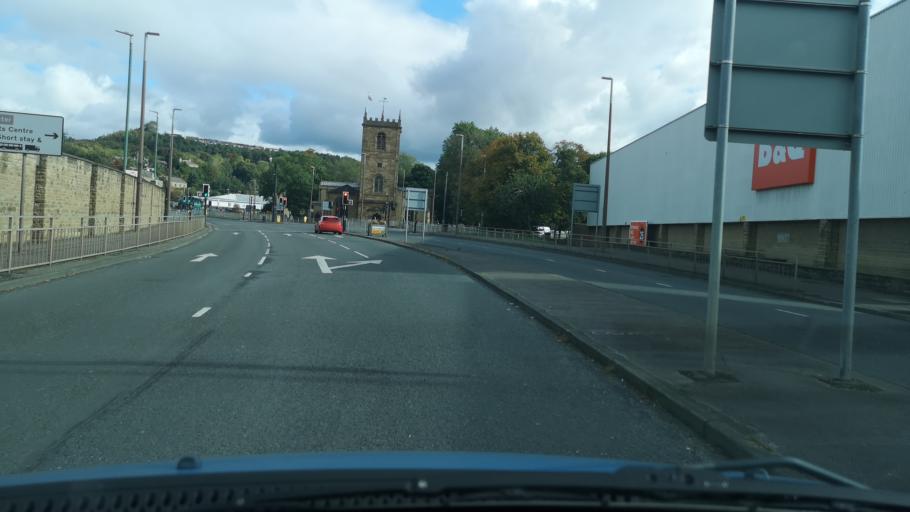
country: GB
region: England
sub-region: Kirklees
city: Dewsbury
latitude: 53.6893
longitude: -1.6317
